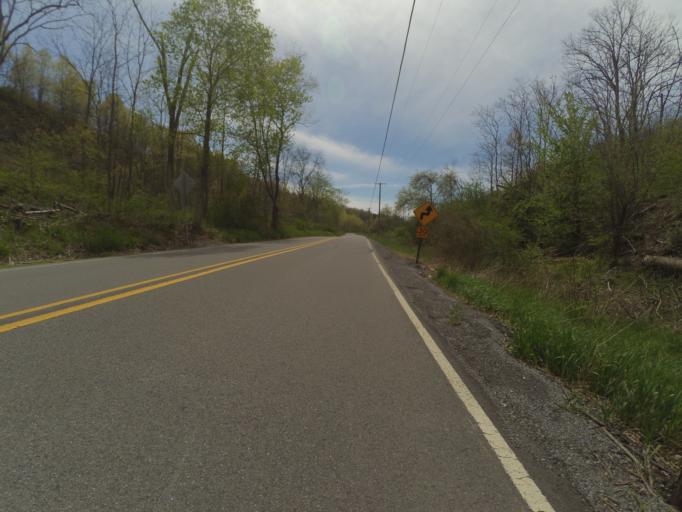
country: US
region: Pennsylvania
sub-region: Blair County
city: Tyrone
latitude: 40.6536
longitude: -78.2237
